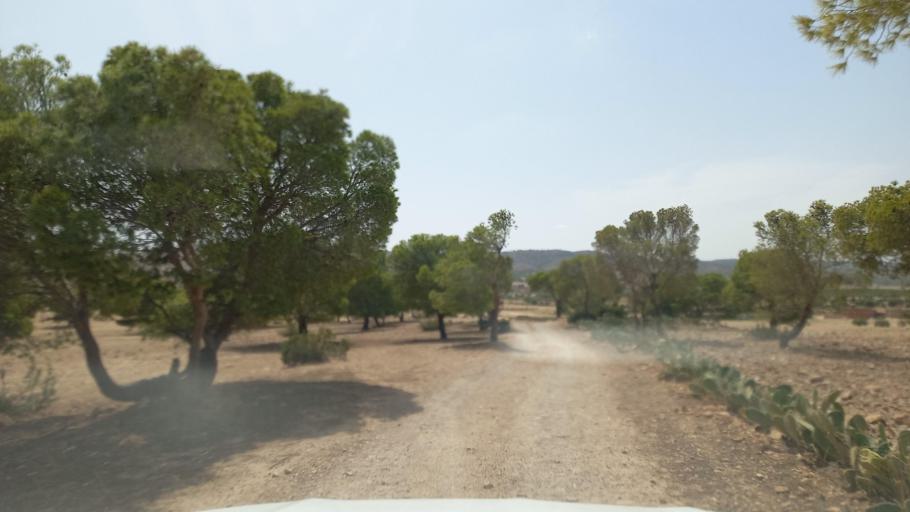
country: TN
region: Al Qasrayn
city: Sbiba
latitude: 35.3978
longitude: 8.9860
